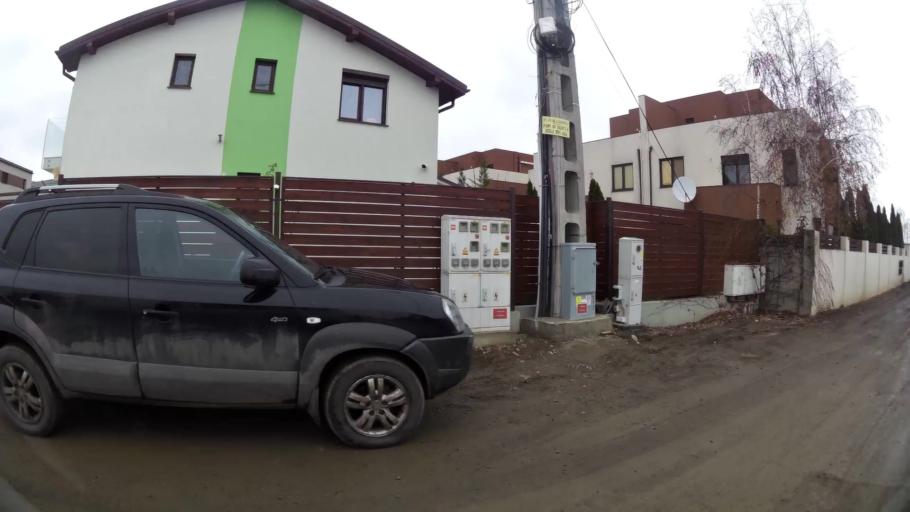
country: RO
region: Ilfov
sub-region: Comuna Otopeni
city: Otopeni
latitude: 44.5556
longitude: 26.0982
